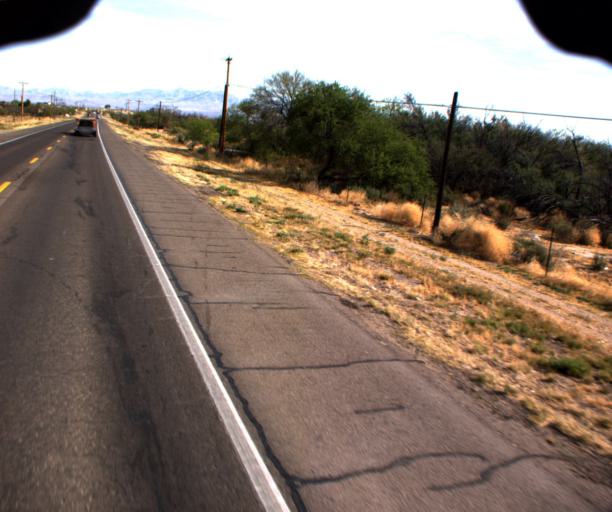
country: US
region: Arizona
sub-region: Graham County
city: Cactus Flat
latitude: 32.7691
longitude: -109.7163
